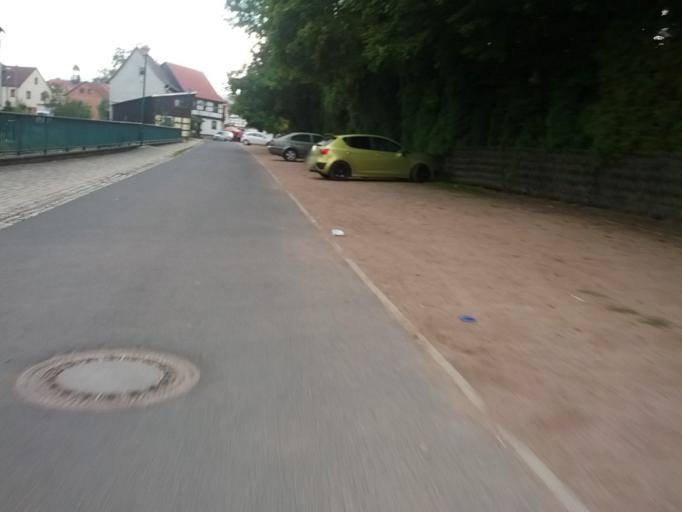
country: DE
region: Thuringia
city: Thal
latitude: 50.9426
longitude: 10.3912
